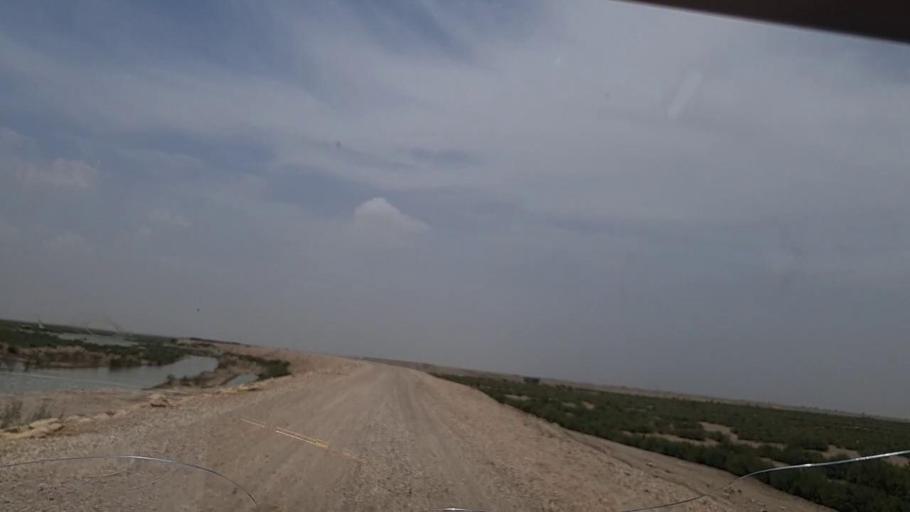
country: PK
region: Sindh
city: Bhan
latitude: 26.5076
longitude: 67.6296
